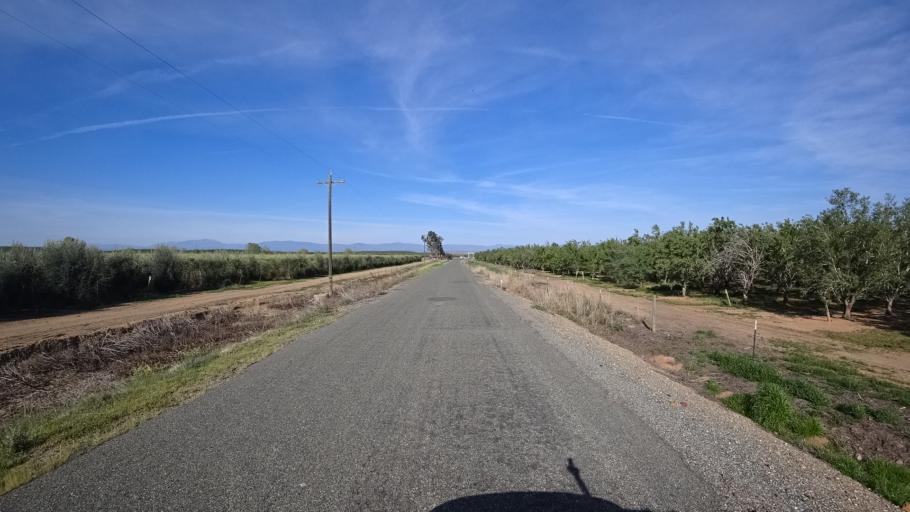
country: US
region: California
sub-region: Glenn County
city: Orland
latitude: 39.6687
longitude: -122.2874
